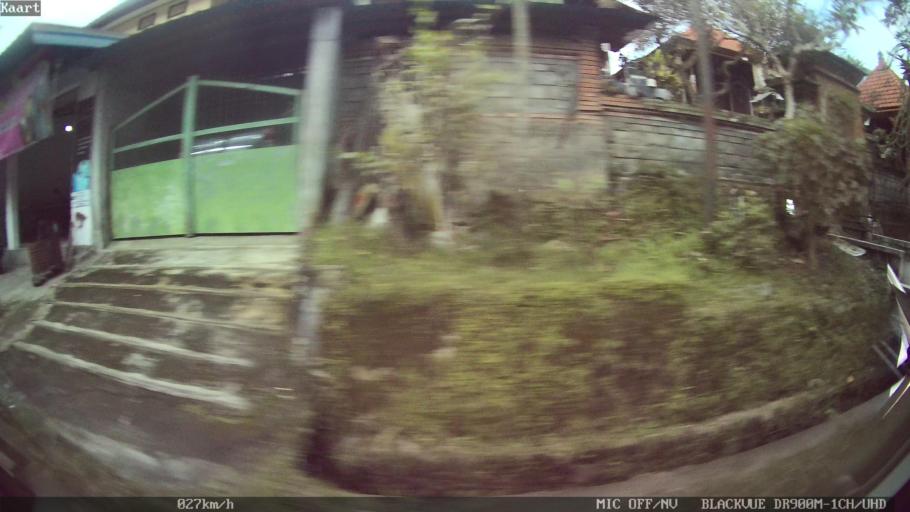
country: ID
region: Bali
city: Banjar Madangan Kaja
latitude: -8.4808
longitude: 115.3215
